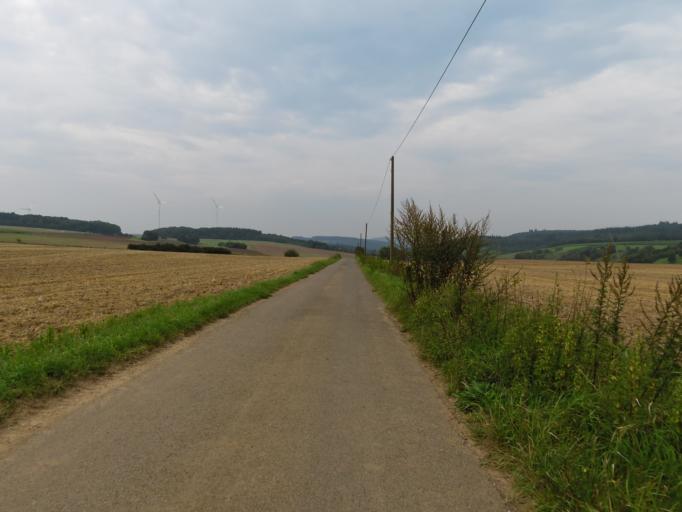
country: DE
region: Rheinland-Pfalz
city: Furfeld
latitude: 49.7766
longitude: 7.8759
